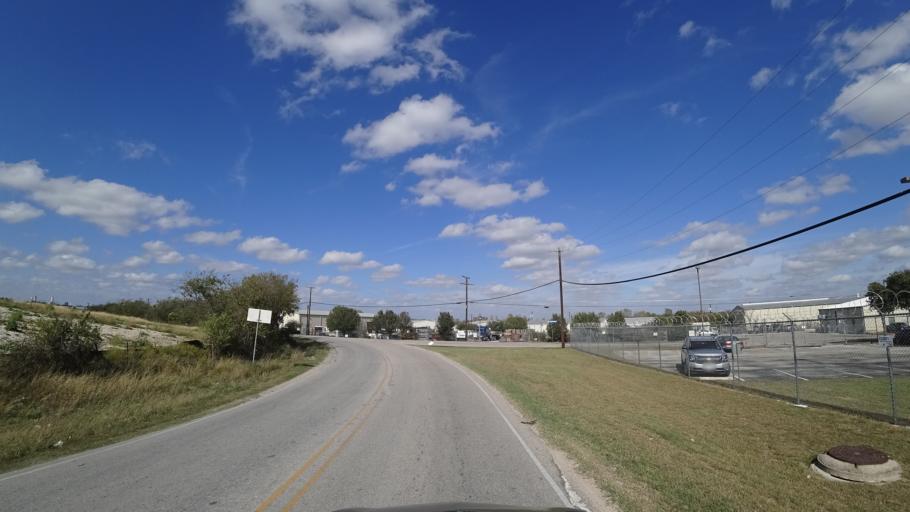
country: US
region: Texas
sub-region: Travis County
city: Windemere
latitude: 30.4645
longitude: -97.6591
